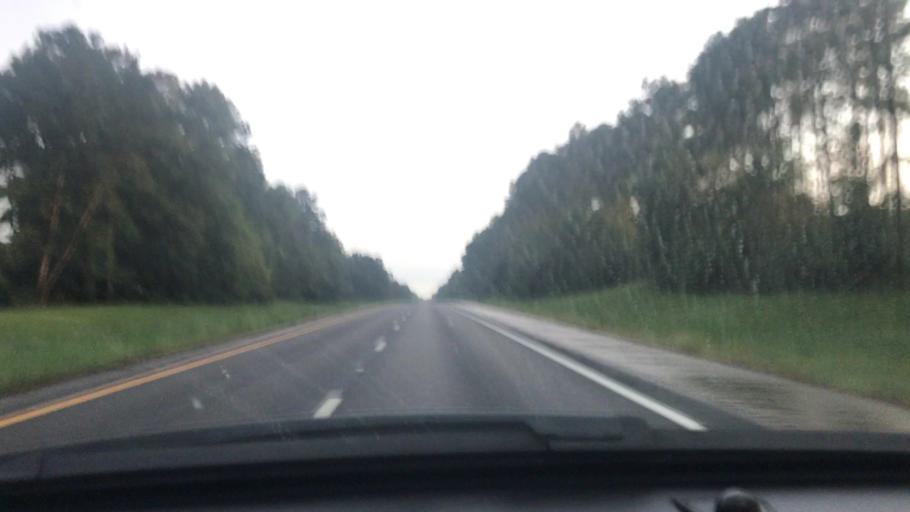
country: US
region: Mississippi
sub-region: Pike County
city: Magnolia
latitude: 31.0894
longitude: -90.4893
